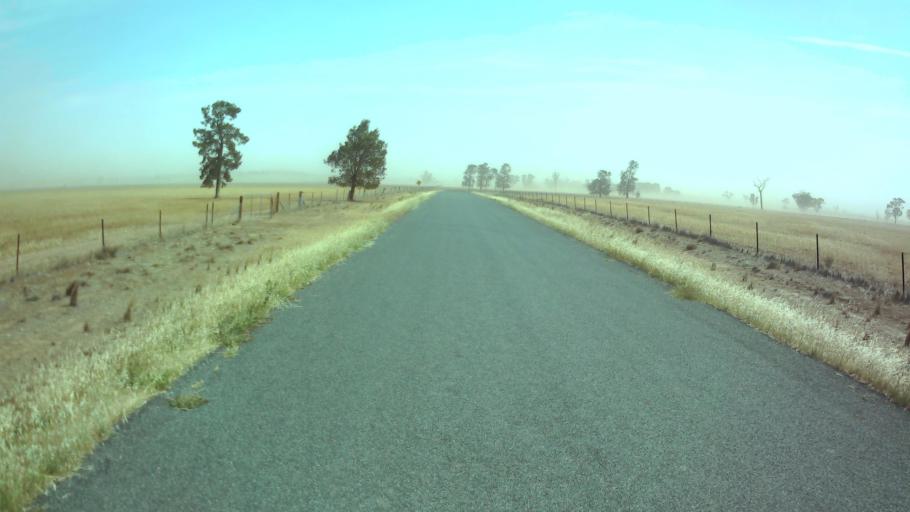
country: AU
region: New South Wales
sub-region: Weddin
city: Grenfell
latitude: -33.7399
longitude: 147.9929
